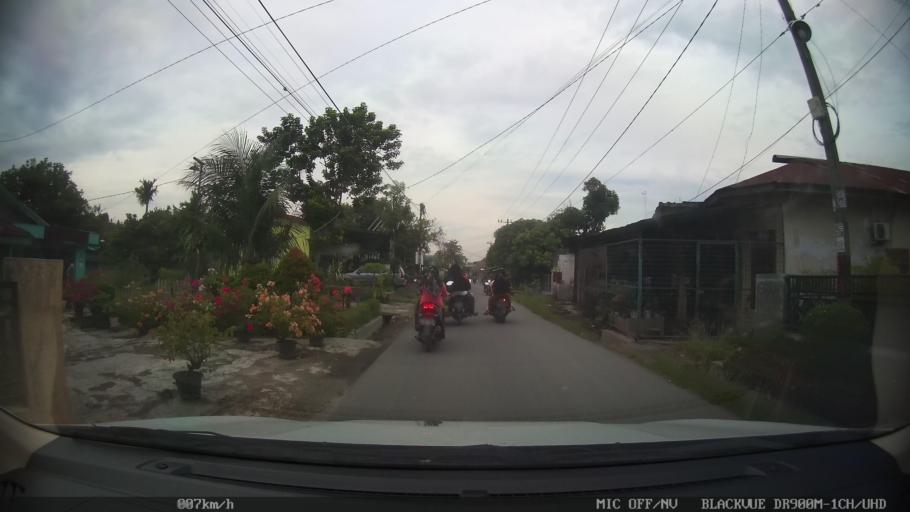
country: ID
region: North Sumatra
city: Sunggal
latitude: 3.6115
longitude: 98.6011
